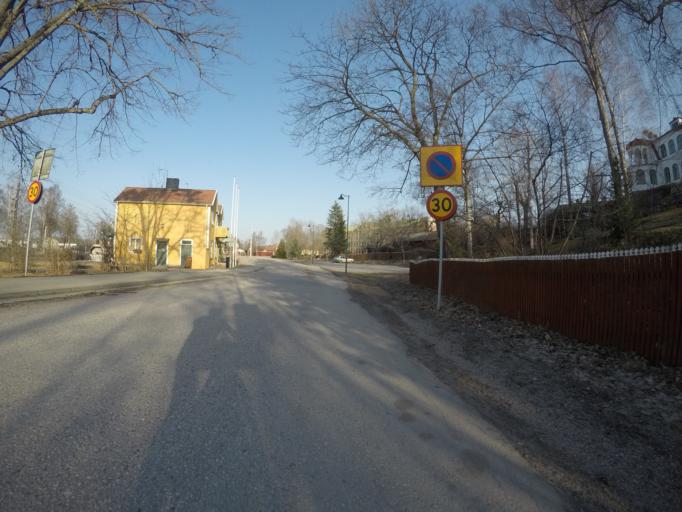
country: SE
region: Vaestmanland
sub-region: Kungsors Kommun
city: Kungsoer
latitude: 59.4273
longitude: 16.0996
